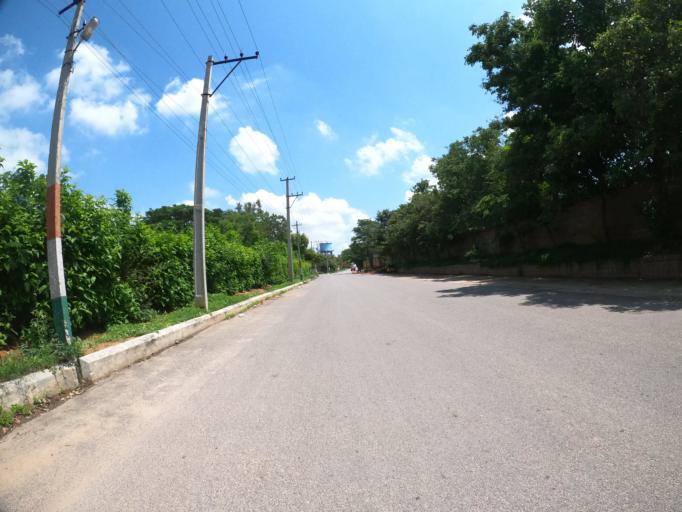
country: IN
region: Telangana
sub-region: Medak
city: Serilingampalle
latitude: 17.3888
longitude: 78.3154
